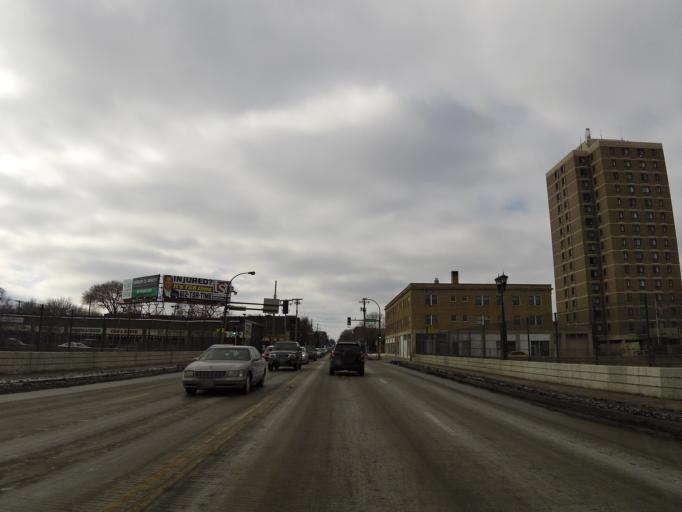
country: US
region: Minnesota
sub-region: Hennepin County
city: Minneapolis
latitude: 44.9627
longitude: -93.2694
